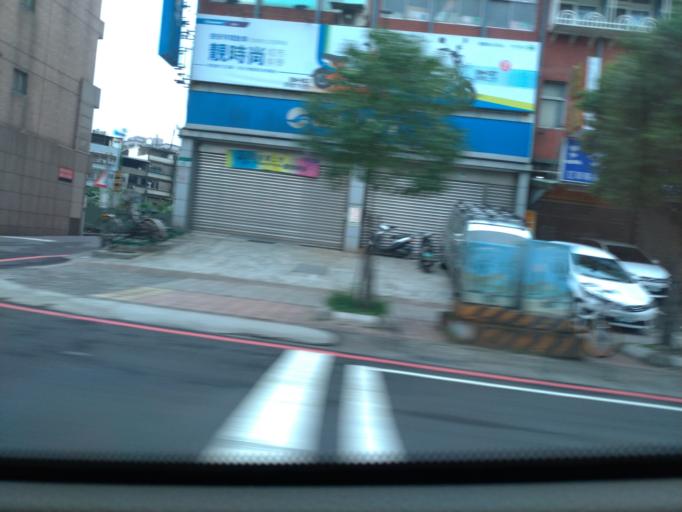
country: TW
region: Taiwan
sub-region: Taoyuan
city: Taoyuan
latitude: 24.9373
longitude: 121.3729
